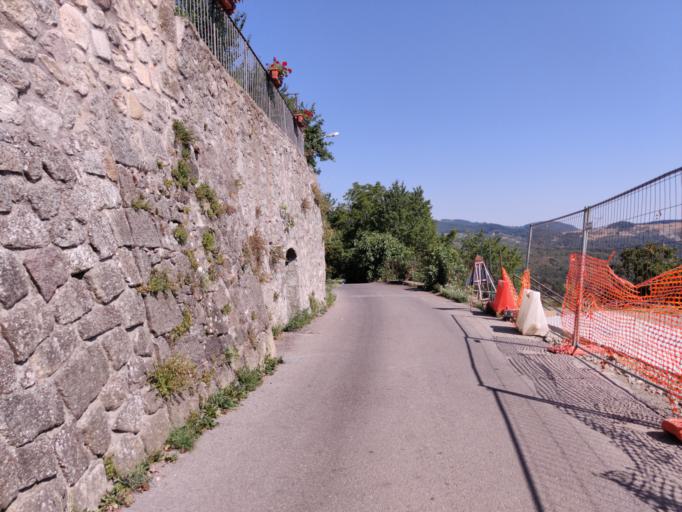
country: IT
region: Tuscany
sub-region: Provincia di Siena
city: Abbadia San Salvatore
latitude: 42.8815
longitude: 11.6790
